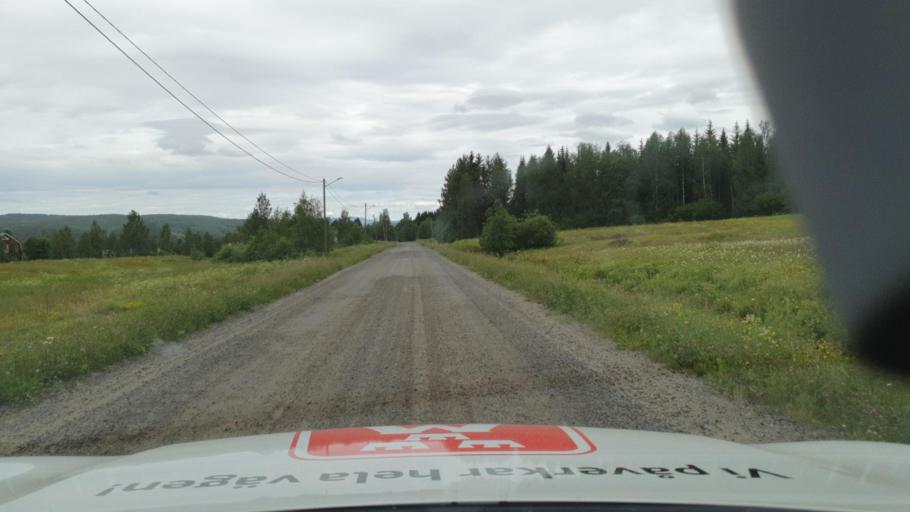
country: SE
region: Vaesterbotten
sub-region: Bjurholms Kommun
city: Bjurholm
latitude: 63.7871
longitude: 19.3737
